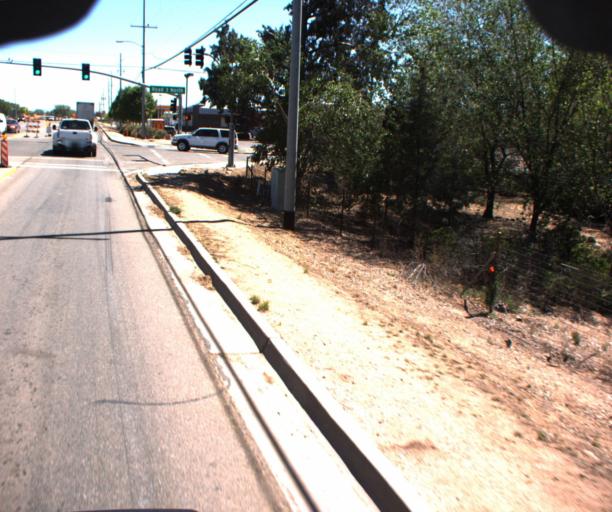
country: US
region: Arizona
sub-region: Yavapai County
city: Chino Valley
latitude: 34.7750
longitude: -112.4529
